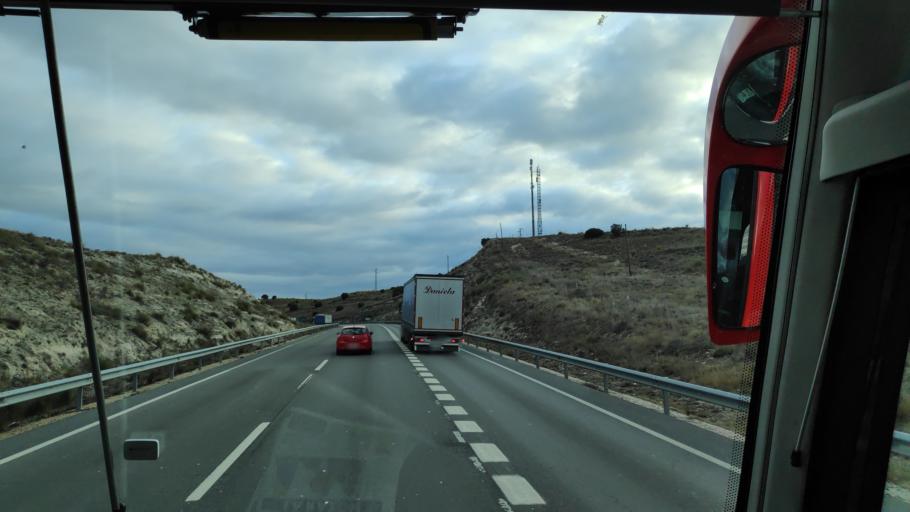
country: ES
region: Madrid
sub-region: Provincia de Madrid
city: Tielmes
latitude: 40.2028
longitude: -3.3149
